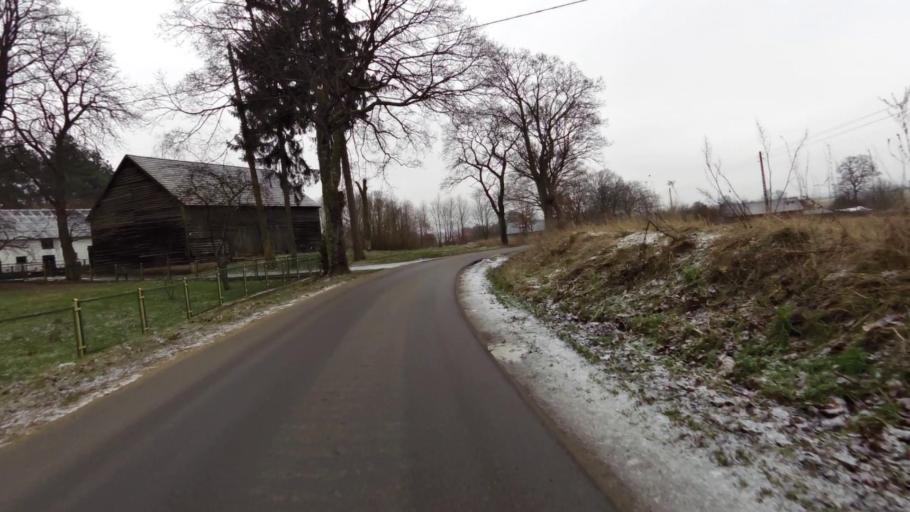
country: PL
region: West Pomeranian Voivodeship
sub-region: Powiat szczecinecki
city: Szczecinek
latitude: 53.6642
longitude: 16.6246
